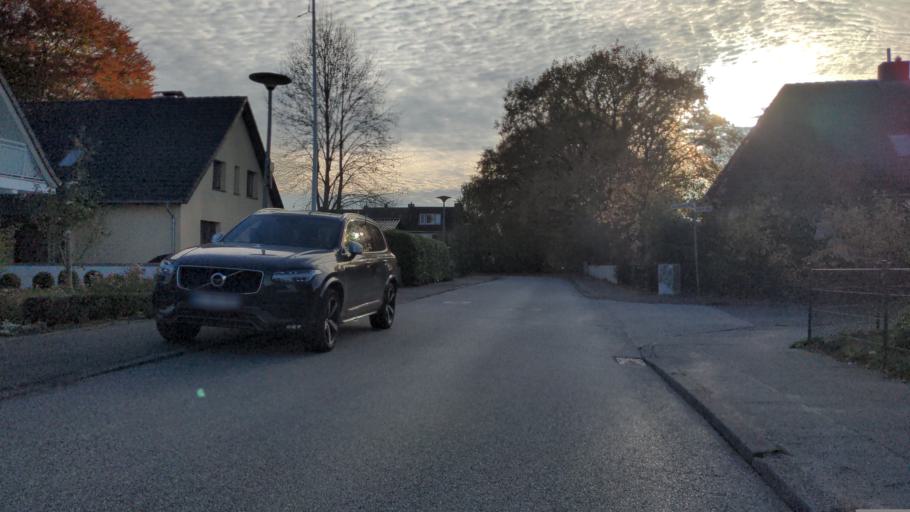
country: DE
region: Schleswig-Holstein
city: Gross Gronau
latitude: 53.8413
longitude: 10.7437
